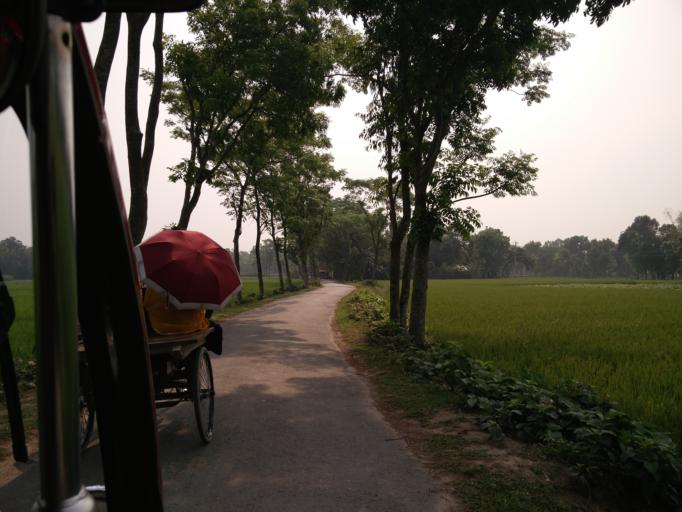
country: BD
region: Dhaka
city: Muktagacha
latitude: 24.9138
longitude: 90.2260
